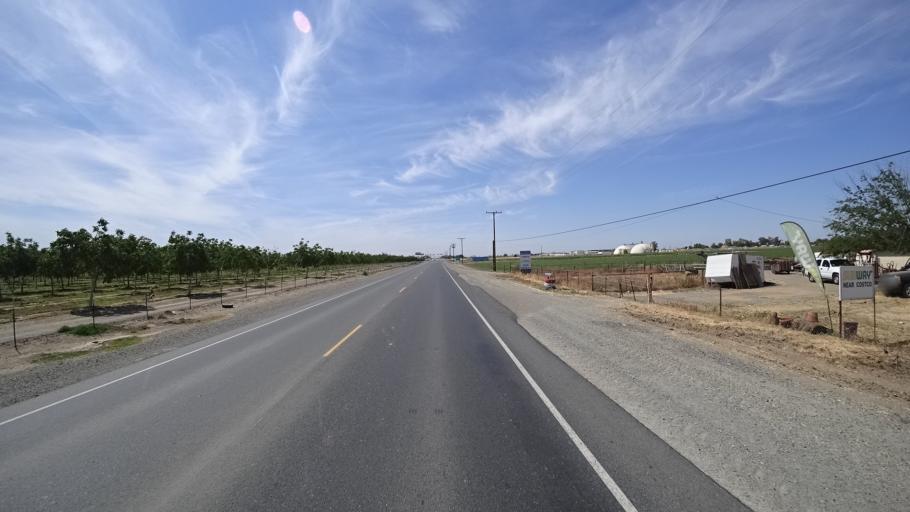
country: US
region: California
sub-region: Kings County
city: Hanford
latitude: 36.3351
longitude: -119.6010
